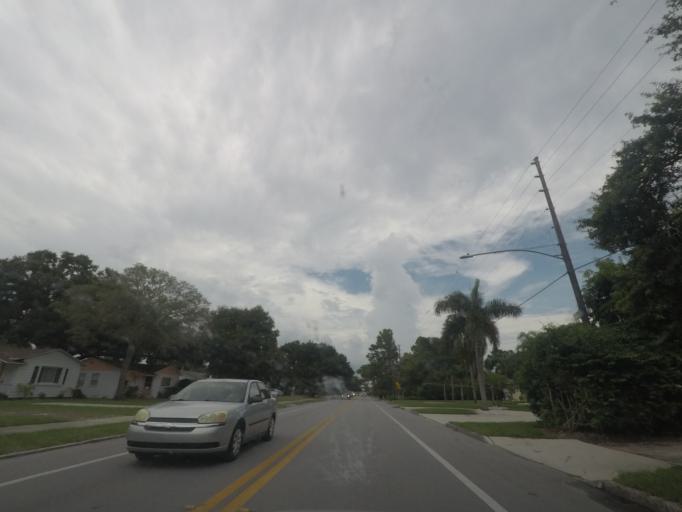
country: US
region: Florida
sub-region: Pinellas County
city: West and East Lealman
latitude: 27.7991
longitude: -82.6892
